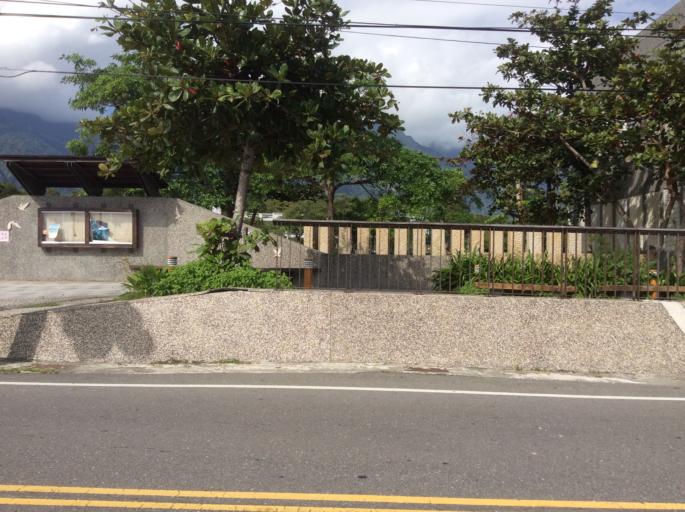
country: TW
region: Taiwan
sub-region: Taitung
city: Taitung
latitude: 23.3154
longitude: 121.4526
